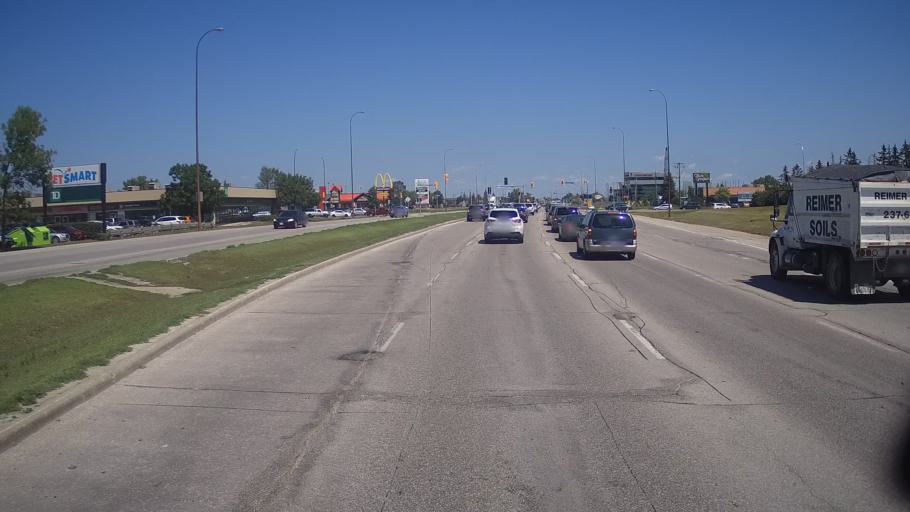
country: CA
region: Manitoba
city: Winnipeg
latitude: 49.9011
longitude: -97.0674
